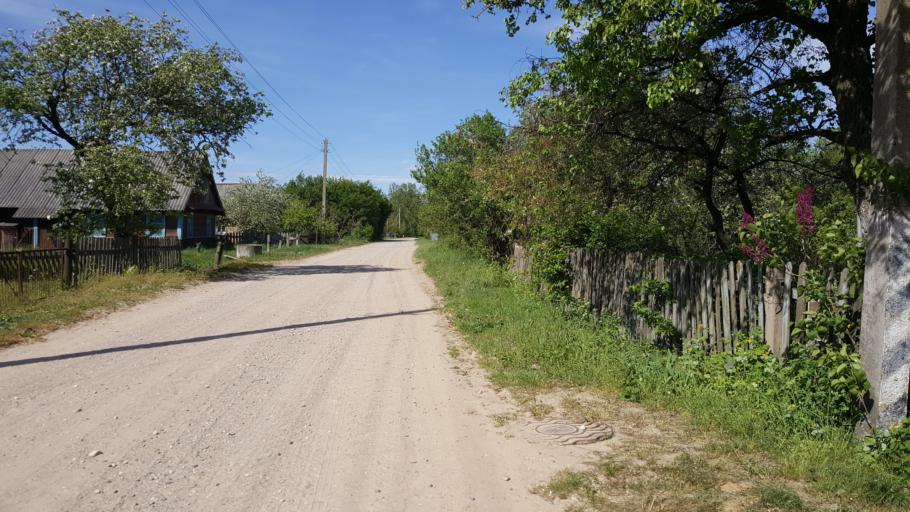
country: BY
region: Brest
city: Zhabinka
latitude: 52.3203
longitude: 24.0435
